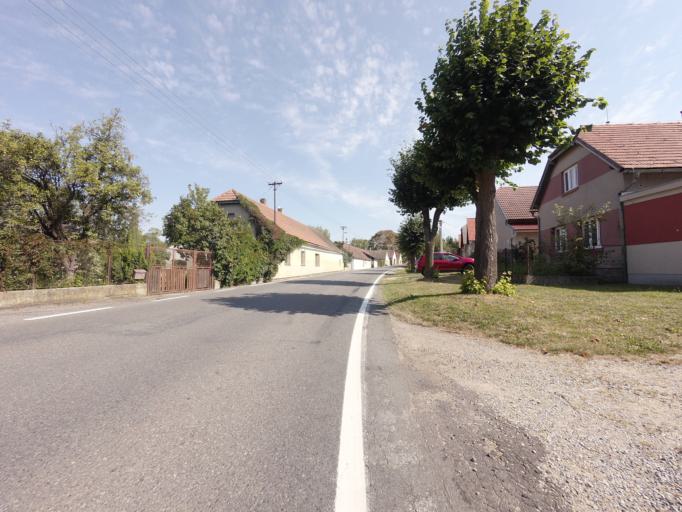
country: CZ
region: Jihocesky
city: Bernartice
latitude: 49.3906
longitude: 14.3582
